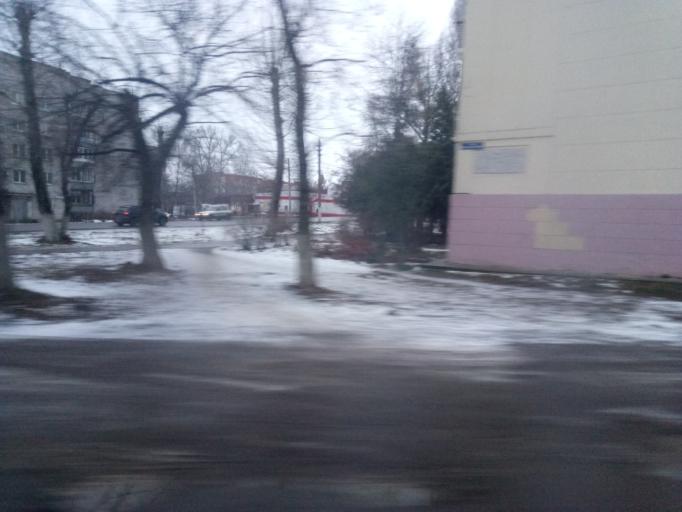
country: RU
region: Tula
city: Tula
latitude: 54.1953
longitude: 37.5641
